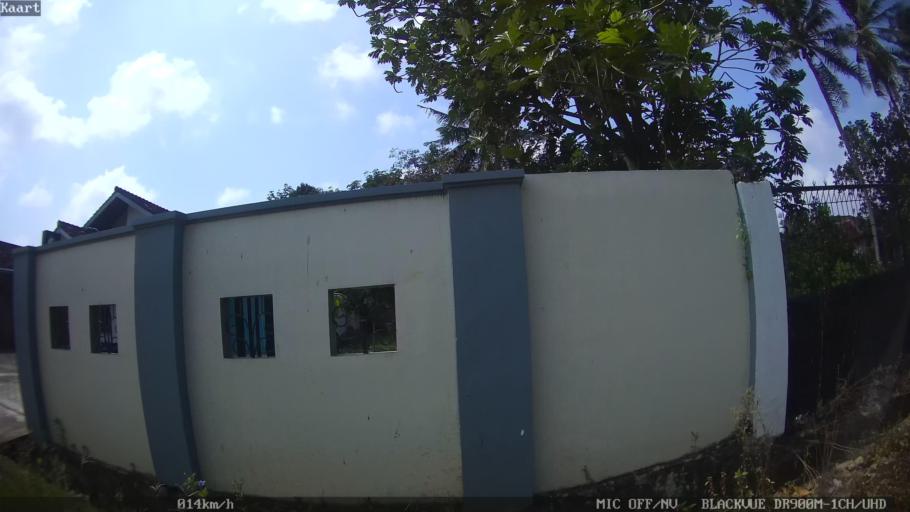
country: ID
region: Lampung
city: Kedaton
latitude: -5.3460
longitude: 105.2892
